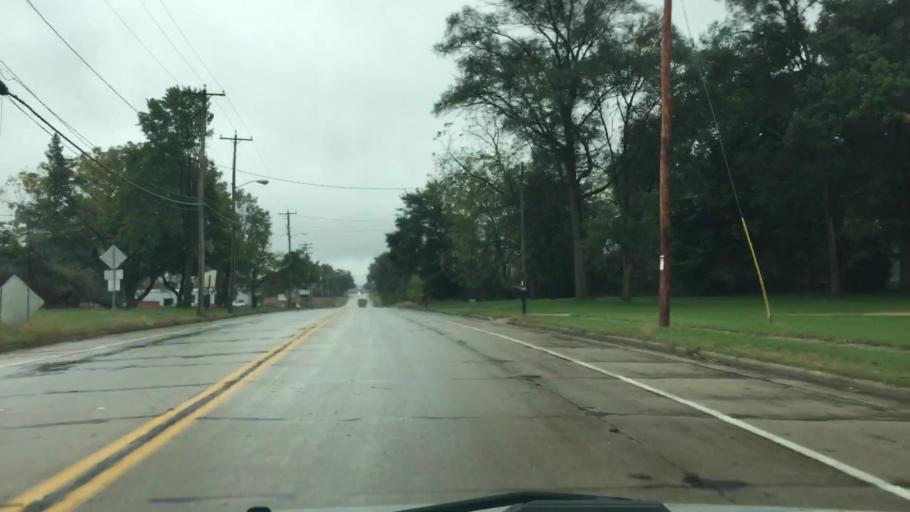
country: US
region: Wisconsin
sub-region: Walworth County
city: Whitewater
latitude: 42.8302
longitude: -88.7099
